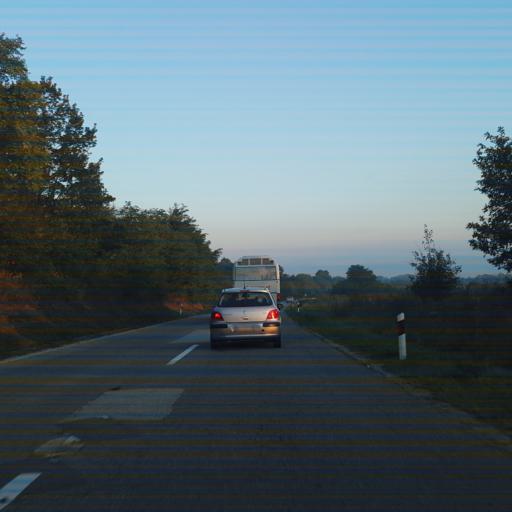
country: RS
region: Central Serbia
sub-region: Zajecarski Okrug
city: Zajecar
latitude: 43.9653
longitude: 22.2961
